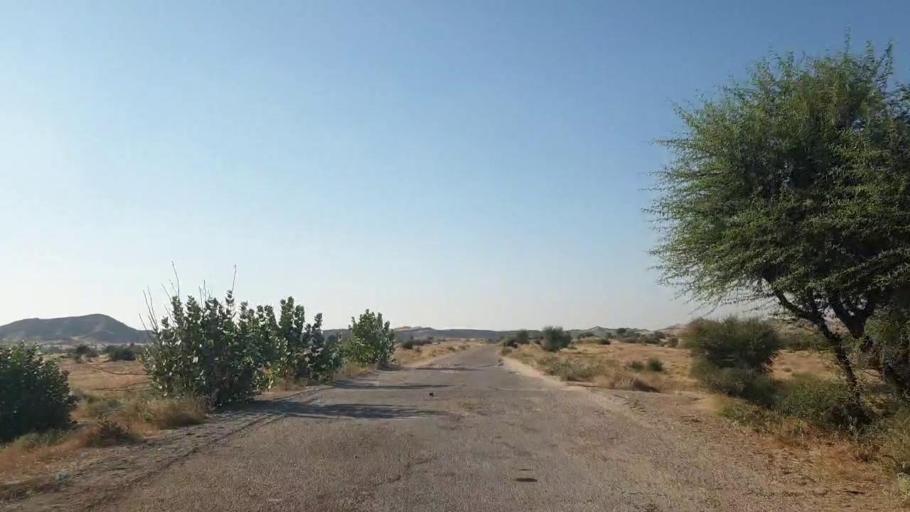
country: PK
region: Sindh
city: Malir Cantonment
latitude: 25.3923
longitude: 67.5004
